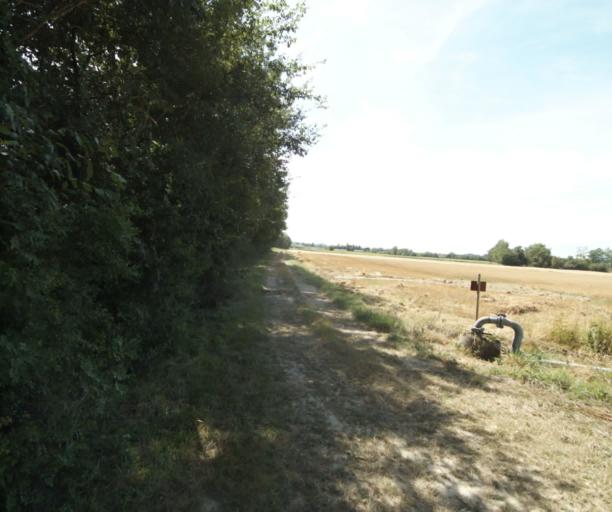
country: FR
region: Midi-Pyrenees
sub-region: Departement du Tarn
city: Puylaurens
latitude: 43.5157
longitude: 2.0257
